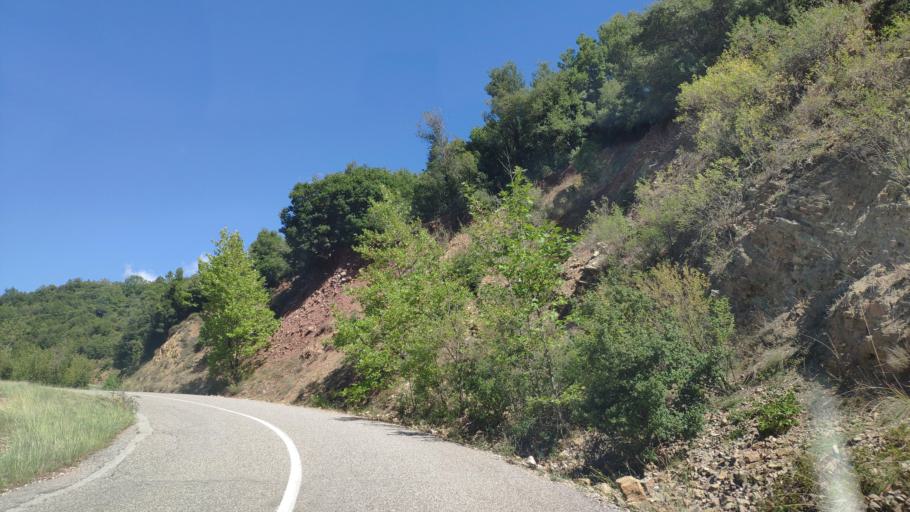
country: GR
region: Central Greece
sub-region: Nomos Evrytanias
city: Kerasochori
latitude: 39.0049
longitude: 21.5940
